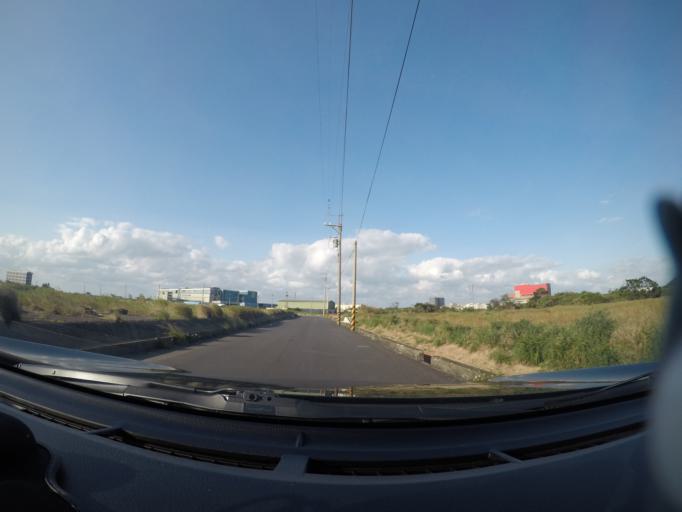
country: TW
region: Taiwan
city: Taoyuan City
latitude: 25.1042
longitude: 121.2523
